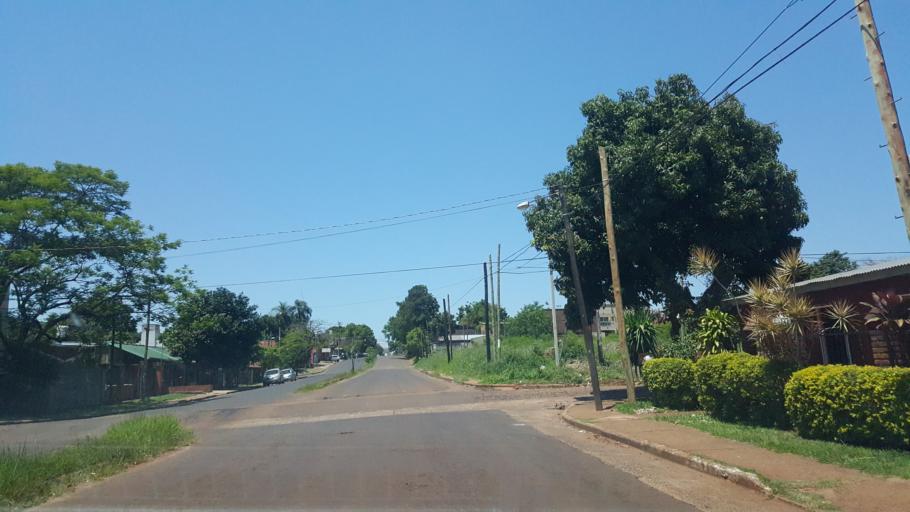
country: AR
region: Misiones
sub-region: Departamento de Capital
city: Posadas
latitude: -27.3820
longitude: -55.9208
